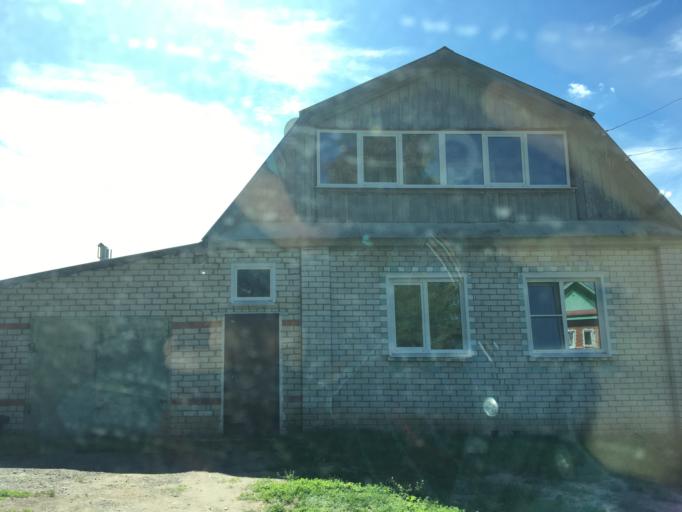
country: RU
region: Nizjnij Novgorod
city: Lyskovo
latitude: 55.9846
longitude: 45.0362
